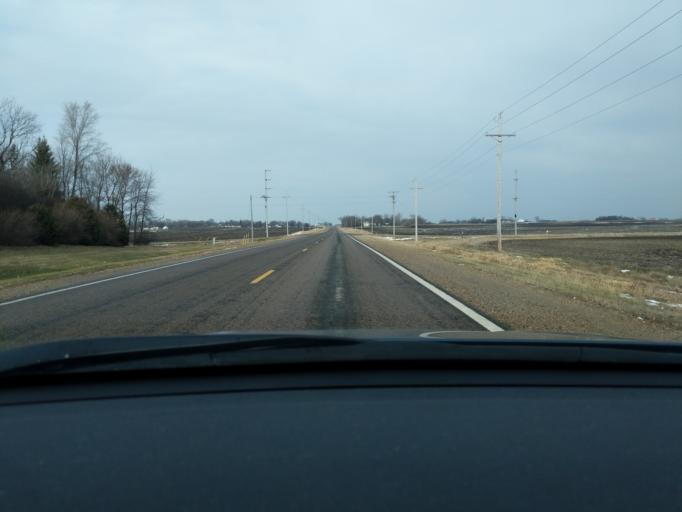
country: US
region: Minnesota
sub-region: Renville County
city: Renville
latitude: 44.7735
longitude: -95.3408
